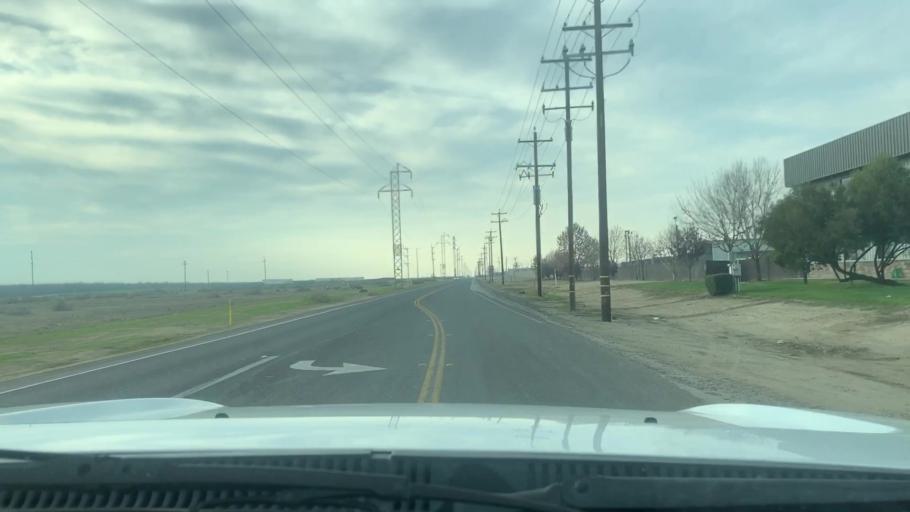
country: US
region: California
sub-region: Kern County
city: Shafter
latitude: 35.4417
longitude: -119.2549
